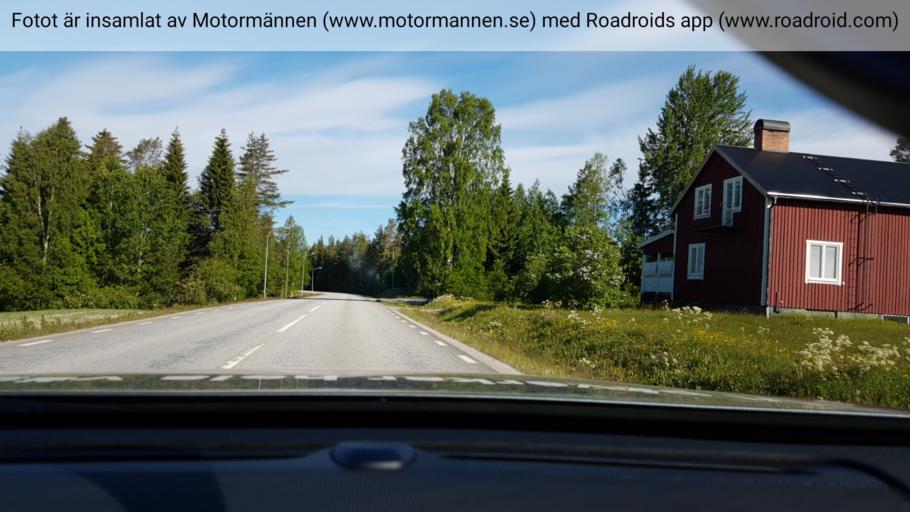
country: SE
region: Vaesterbotten
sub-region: Vindelns Kommun
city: Vindeln
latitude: 64.1111
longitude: 19.5846
